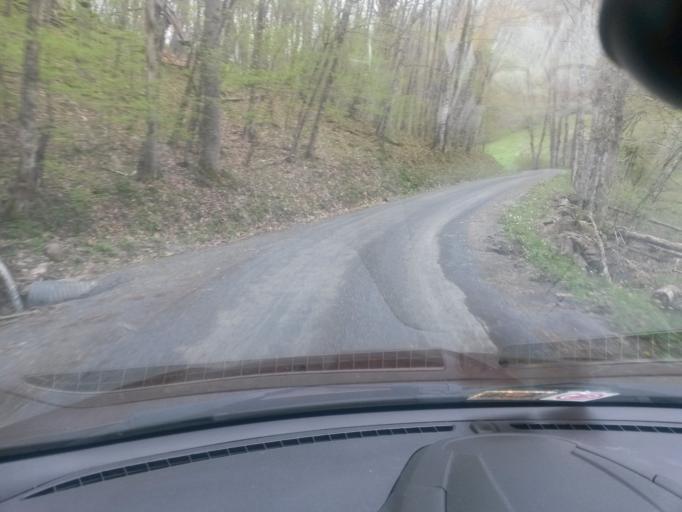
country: US
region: West Virginia
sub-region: Nicholas County
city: Richwood
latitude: 38.0659
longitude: -80.3327
